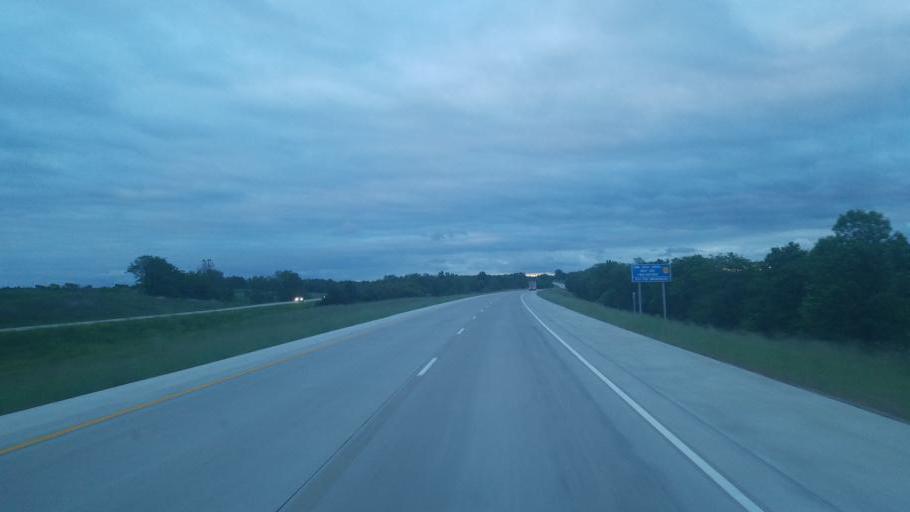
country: US
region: Iowa
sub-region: Decatur County
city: Lamoni
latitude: 40.5918
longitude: -93.9194
